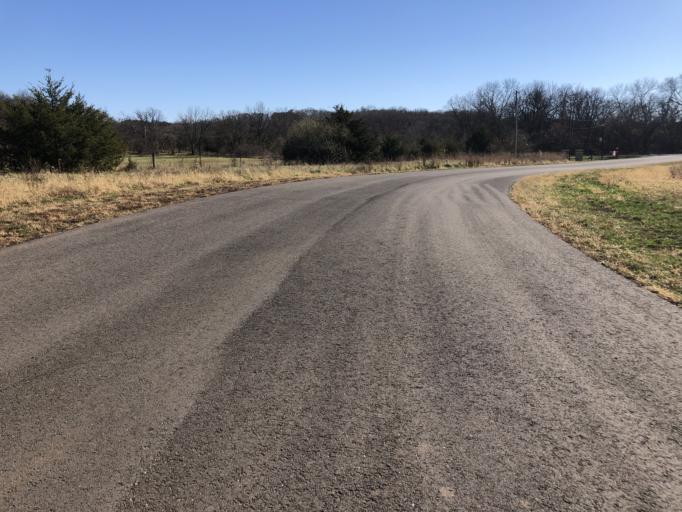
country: US
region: Kansas
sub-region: Johnson County
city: Gardner
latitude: 38.8705
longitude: -94.9497
